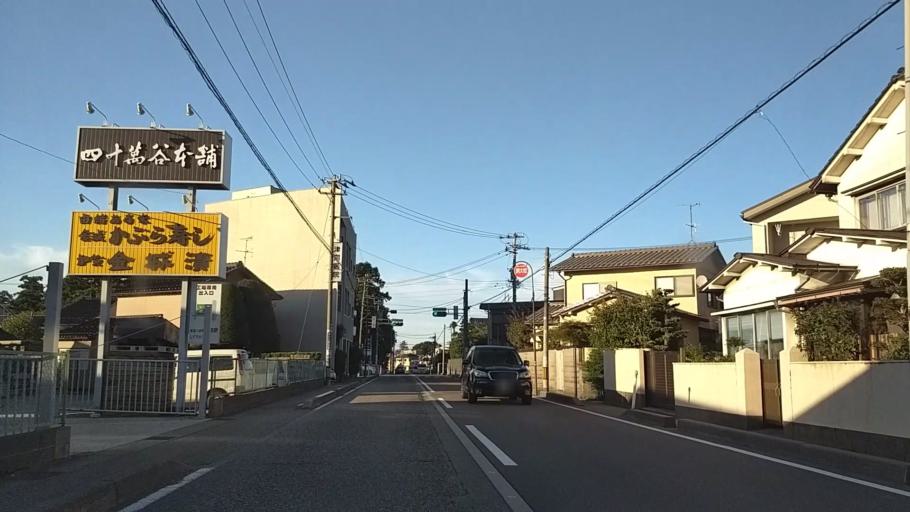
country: JP
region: Ishikawa
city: Nonoichi
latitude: 36.5489
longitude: 136.6495
